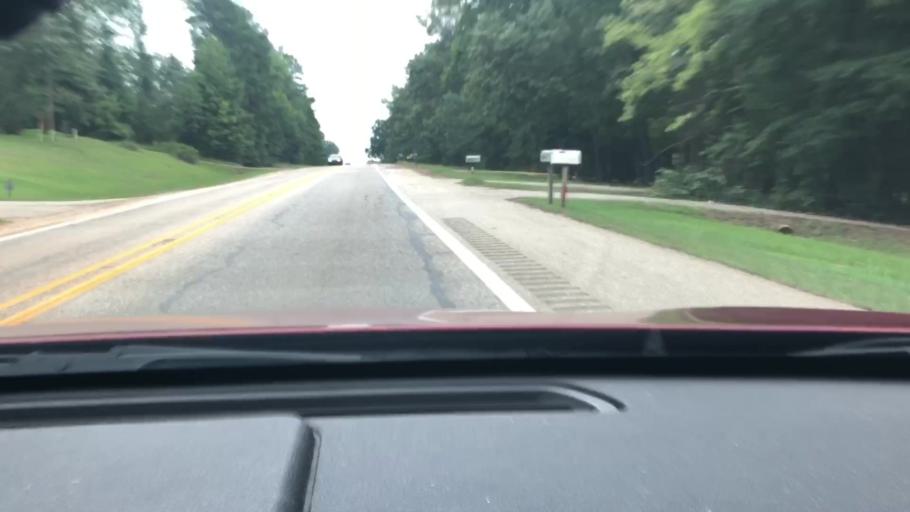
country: US
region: Arkansas
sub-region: Miller County
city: Texarkana
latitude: 33.4293
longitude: -93.9392
